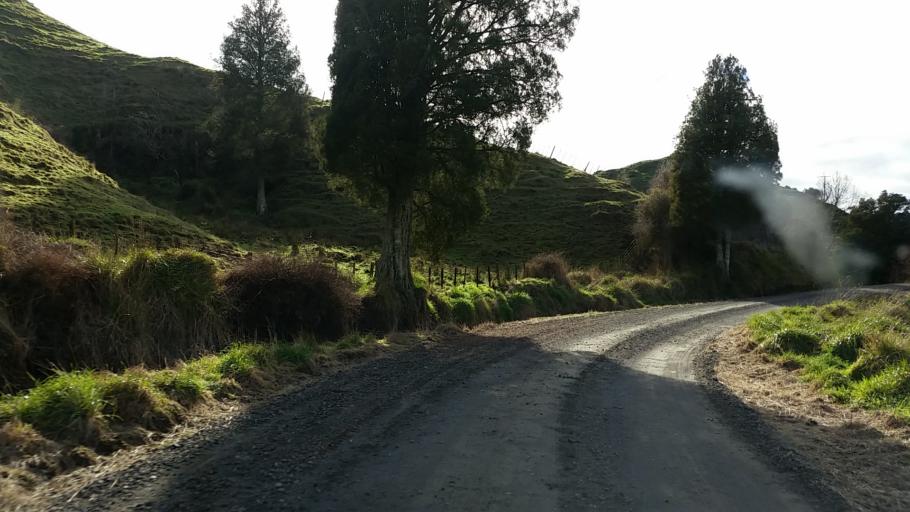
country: NZ
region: Taranaki
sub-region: South Taranaki District
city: Eltham
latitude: -39.2564
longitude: 174.5254
